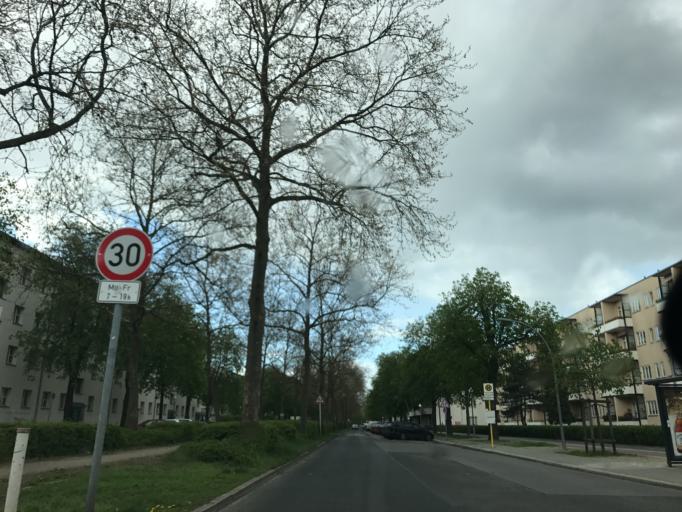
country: DE
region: Berlin
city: Haselhorst
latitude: 52.5448
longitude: 13.2386
